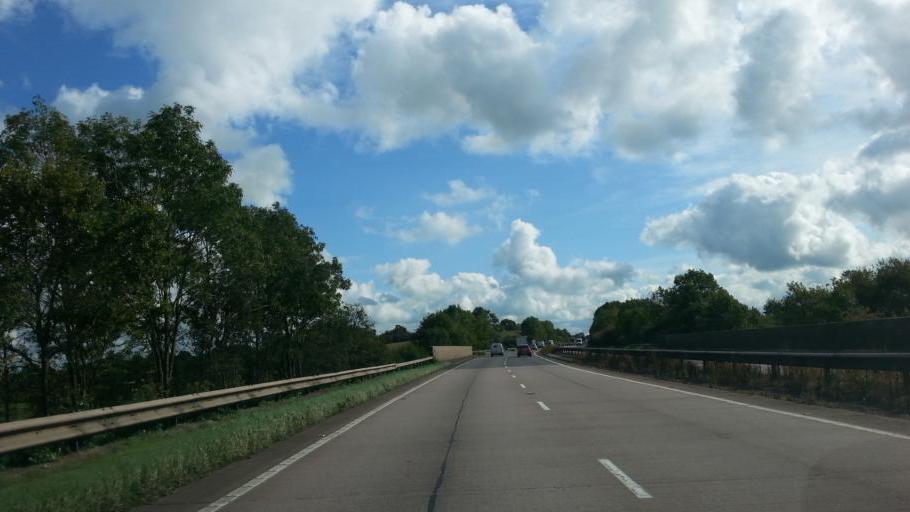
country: GB
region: England
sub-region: Staffordshire
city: Cheadle
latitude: 52.9516
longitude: -2.0193
